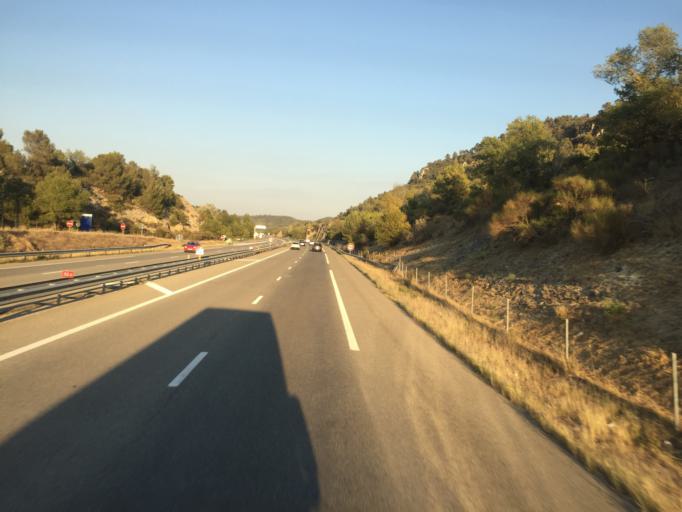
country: FR
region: Provence-Alpes-Cote d'Azur
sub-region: Departement du Vaucluse
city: Beaumont-de-Pertuis
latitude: 43.6909
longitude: 5.6824
